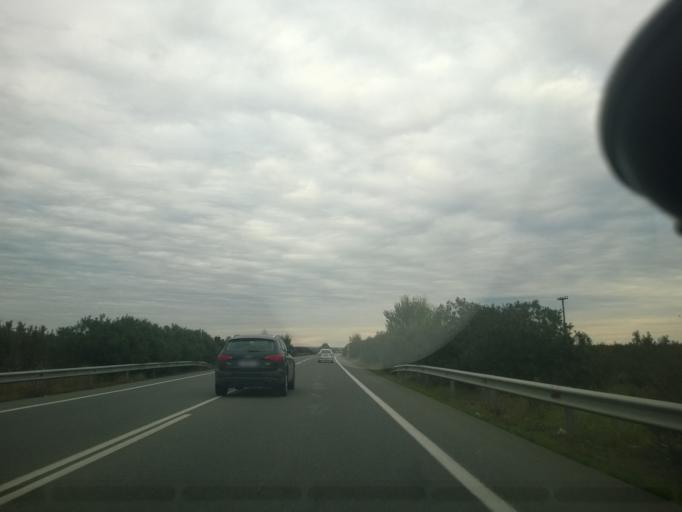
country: GR
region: Central Macedonia
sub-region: Nomos Pellis
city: Kali
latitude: 40.8091
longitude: 22.2235
